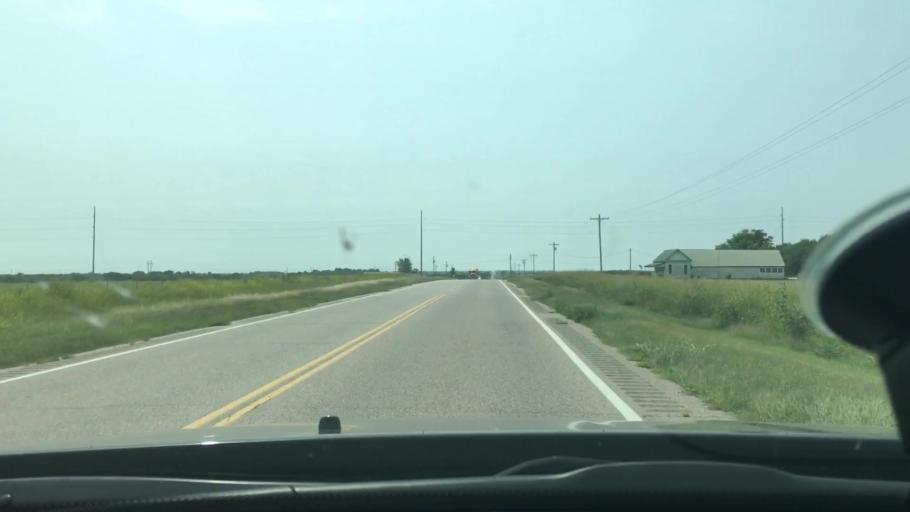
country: US
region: Oklahoma
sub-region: Marshall County
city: Kingston
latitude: 34.0156
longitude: -96.7611
